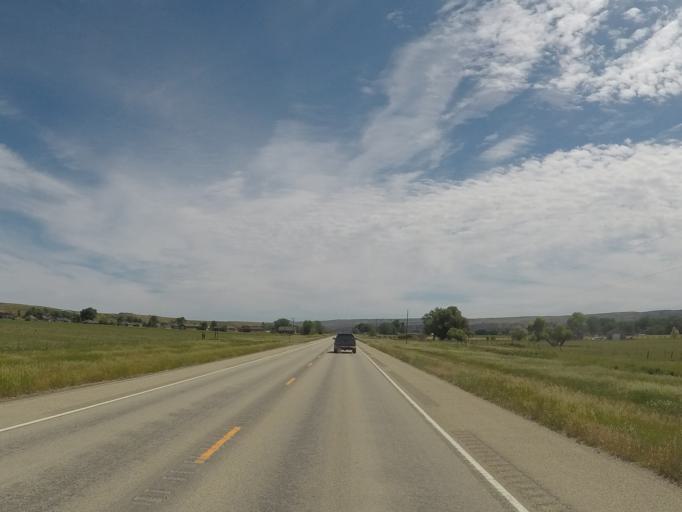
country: US
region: Montana
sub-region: Yellowstone County
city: Laurel
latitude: 45.5130
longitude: -108.8911
